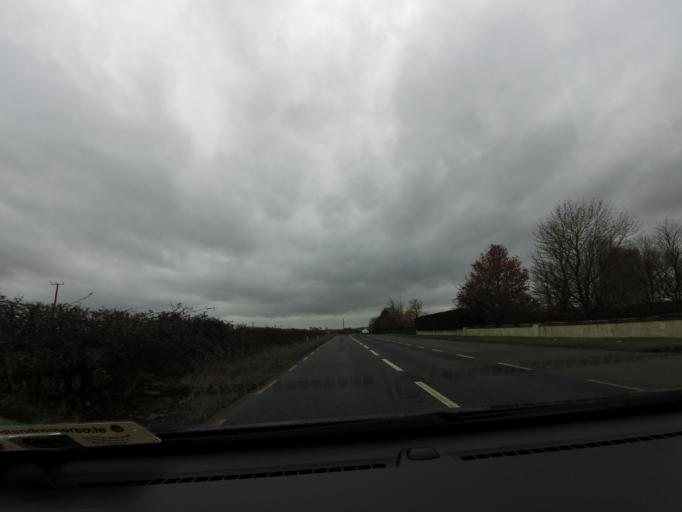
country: IE
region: Leinster
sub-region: Kilkenny
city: Ballyragget
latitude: 52.7621
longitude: -7.3311
